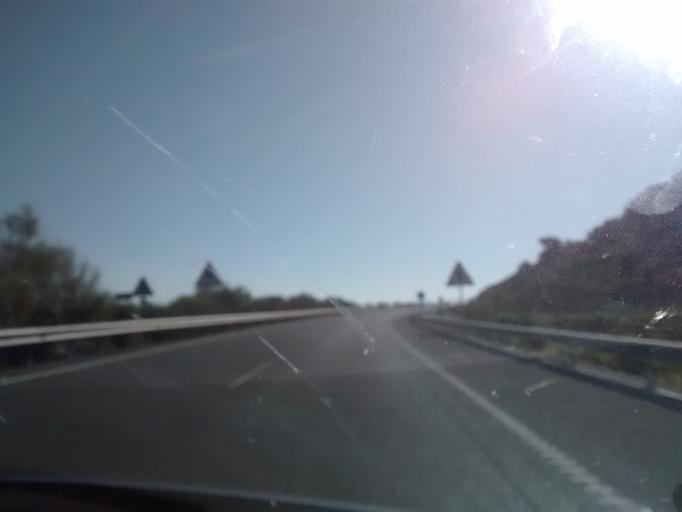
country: ES
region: Andalusia
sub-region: Provincia de Cadiz
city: Paterna de Rivera
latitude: 36.4714
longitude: -5.8057
